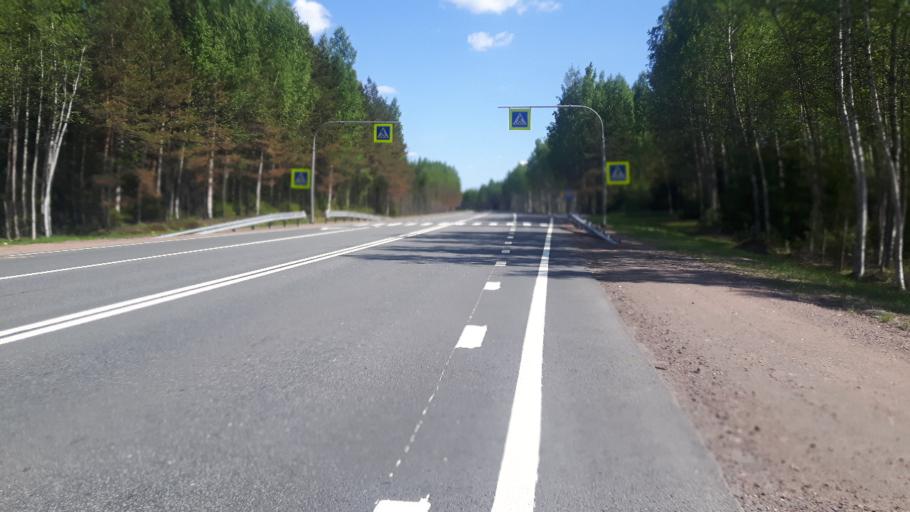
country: FI
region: South Karelia
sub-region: Lappeenranta
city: Ylaemaa
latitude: 60.6256
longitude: 28.2452
